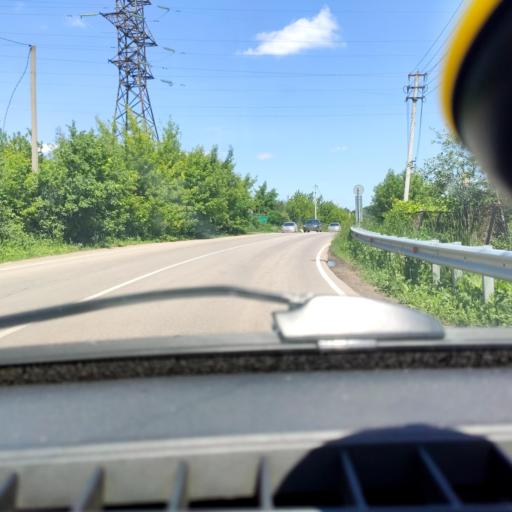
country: RU
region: Samara
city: Zhigulevsk
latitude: 53.3861
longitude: 49.5057
